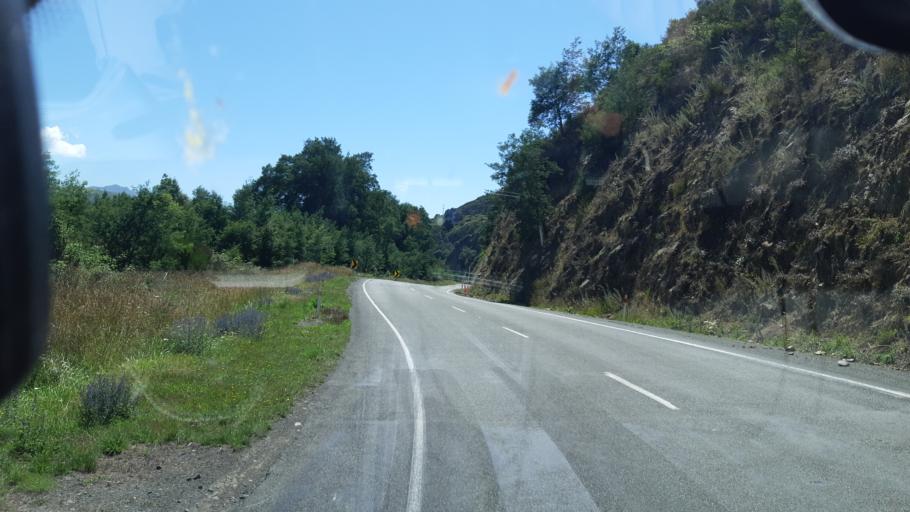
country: NZ
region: Canterbury
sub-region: Kaikoura District
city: Kaikoura
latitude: -42.6338
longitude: 173.3508
